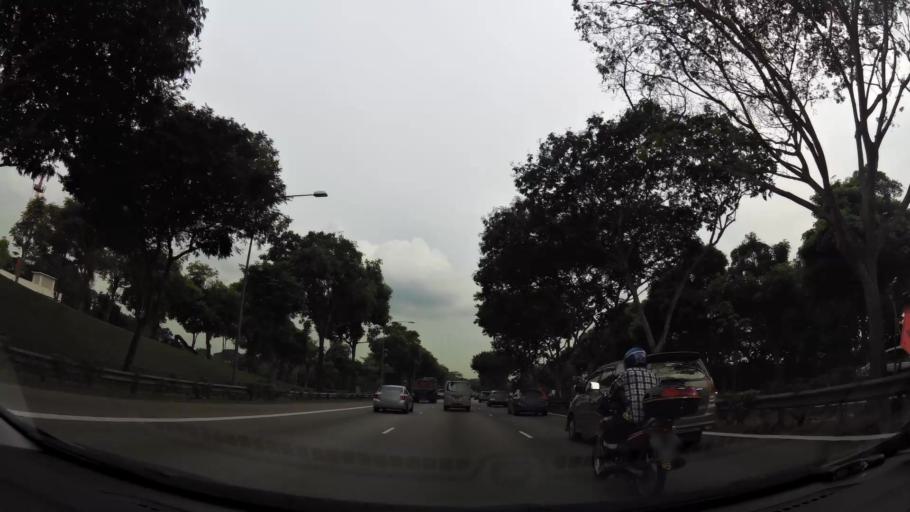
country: MY
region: Johor
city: Johor Bahru
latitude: 1.4042
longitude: 103.8108
